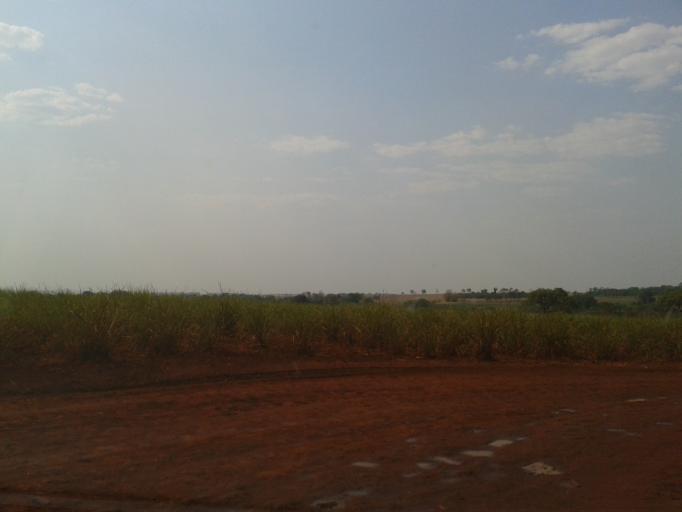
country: BR
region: Minas Gerais
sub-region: Centralina
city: Centralina
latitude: -18.6442
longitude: -49.2438
